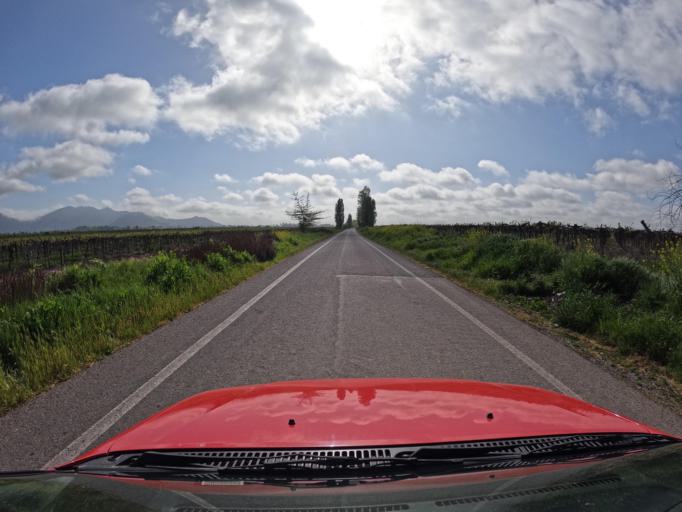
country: CL
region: Maule
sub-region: Provincia de Curico
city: Rauco
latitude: -34.8839
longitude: -71.2506
